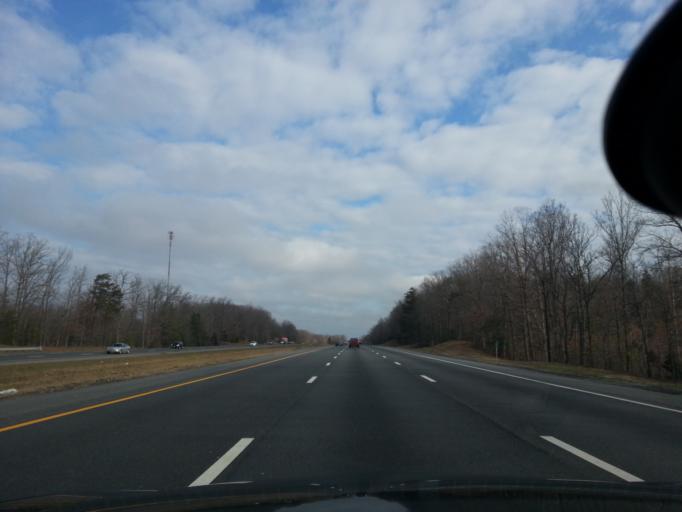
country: US
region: Virginia
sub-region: Spotsylvania County
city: Spotsylvania Courthouse
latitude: 38.0958
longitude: -77.5173
